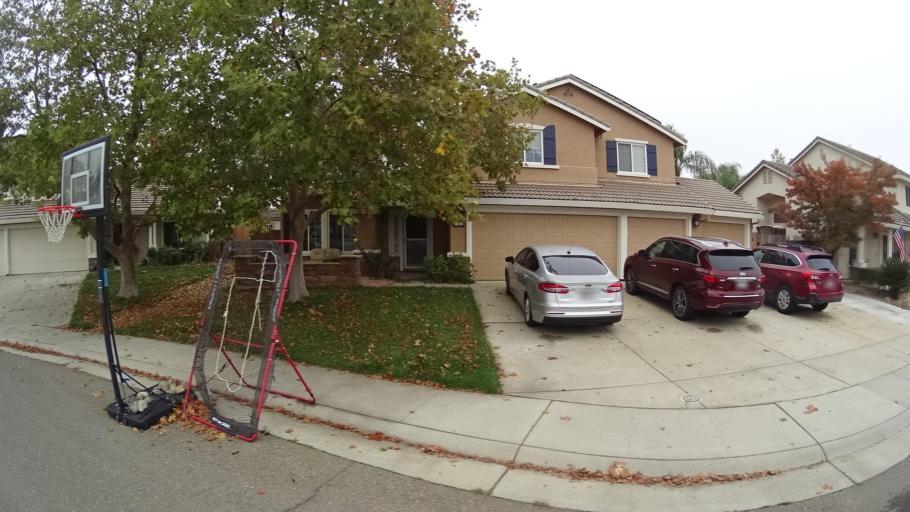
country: US
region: California
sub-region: Sacramento County
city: Elk Grove
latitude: 38.4077
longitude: -121.3432
